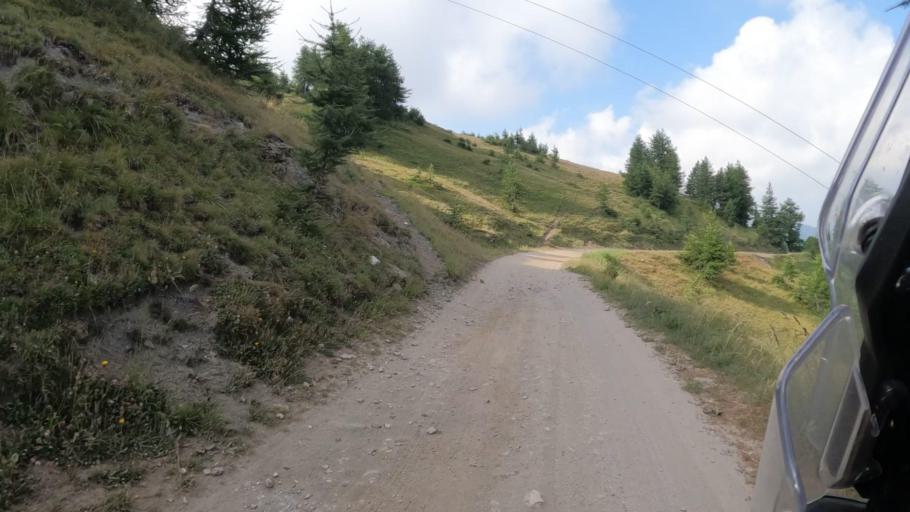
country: IT
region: Piedmont
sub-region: Provincia di Torino
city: Sauze d'Oulx
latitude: 45.0183
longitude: 6.8970
